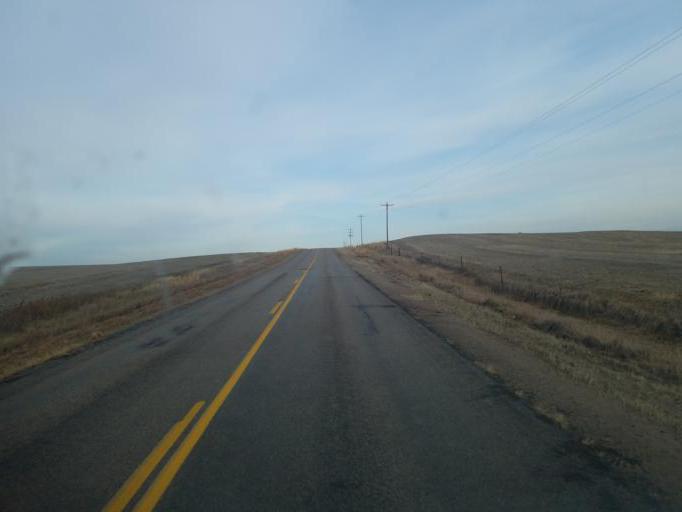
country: US
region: Nebraska
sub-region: Knox County
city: Creighton
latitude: 42.4661
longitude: -98.1781
